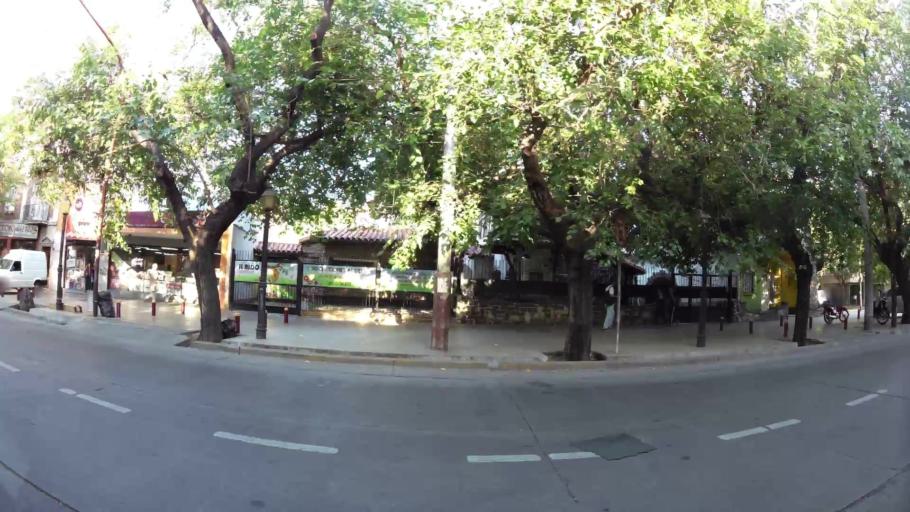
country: AR
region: Mendoza
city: Mendoza
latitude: -32.8962
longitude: -68.8380
